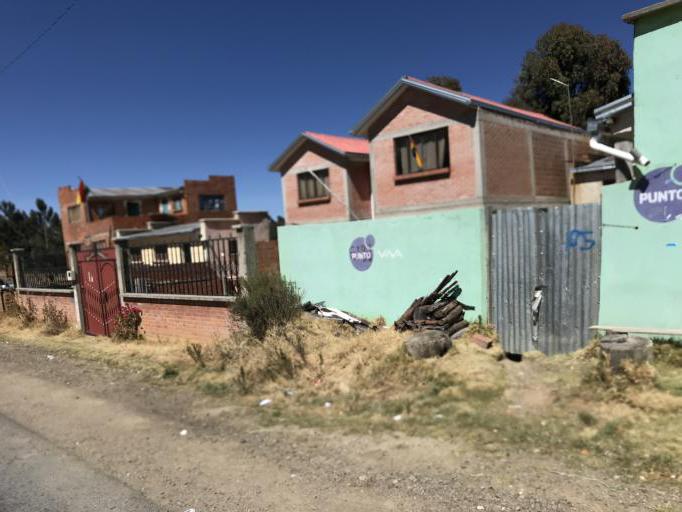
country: BO
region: La Paz
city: Huatajata
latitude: -16.2157
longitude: -68.6669
